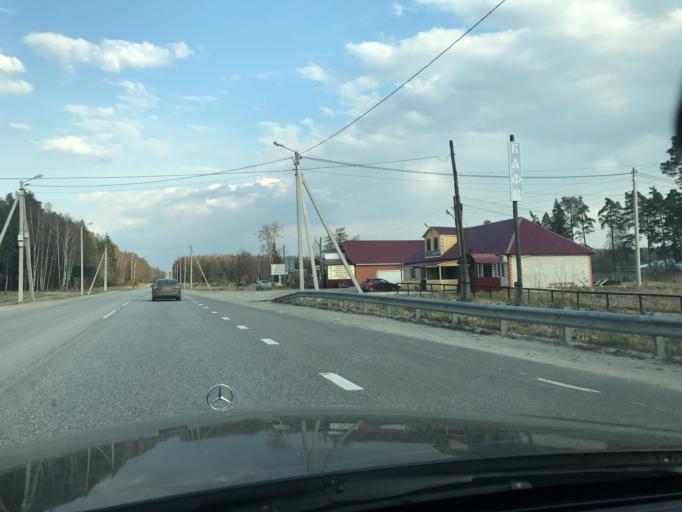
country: RU
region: Vladimir
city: Andreyevo
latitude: 55.9266
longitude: 41.1230
